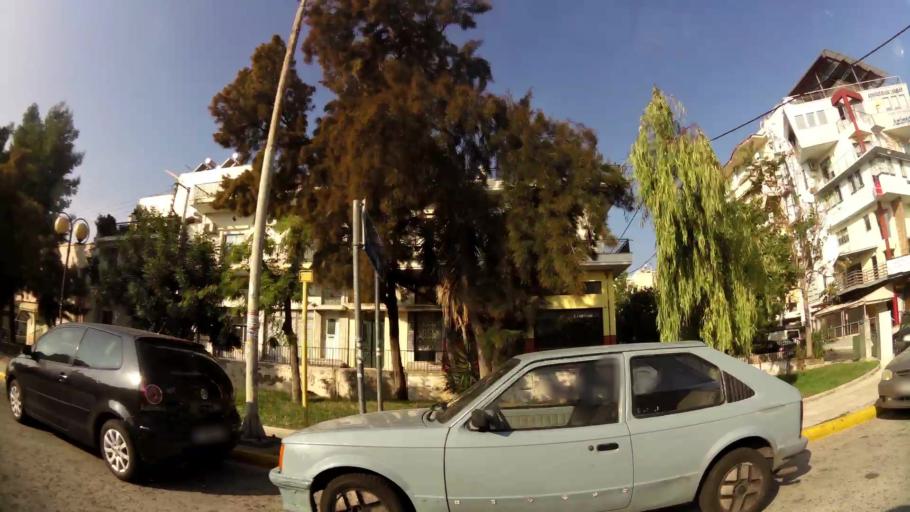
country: GR
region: Attica
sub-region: Nomos Piraios
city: Drapetsona
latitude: 37.9535
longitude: 23.6228
